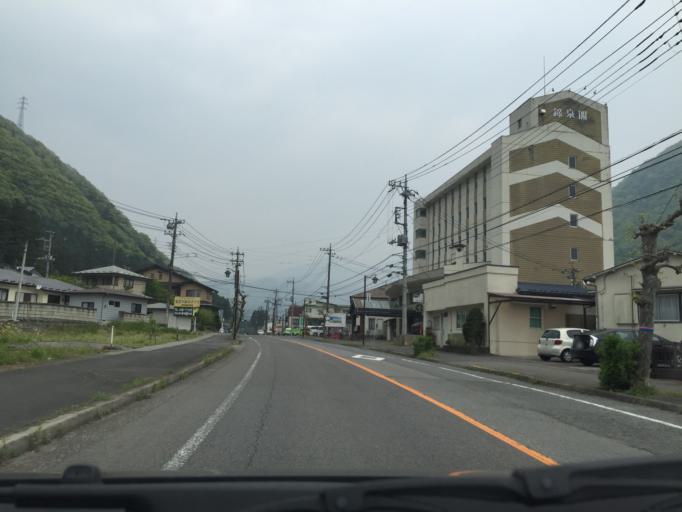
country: JP
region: Tochigi
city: Imaichi
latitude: 36.8295
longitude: 139.7152
